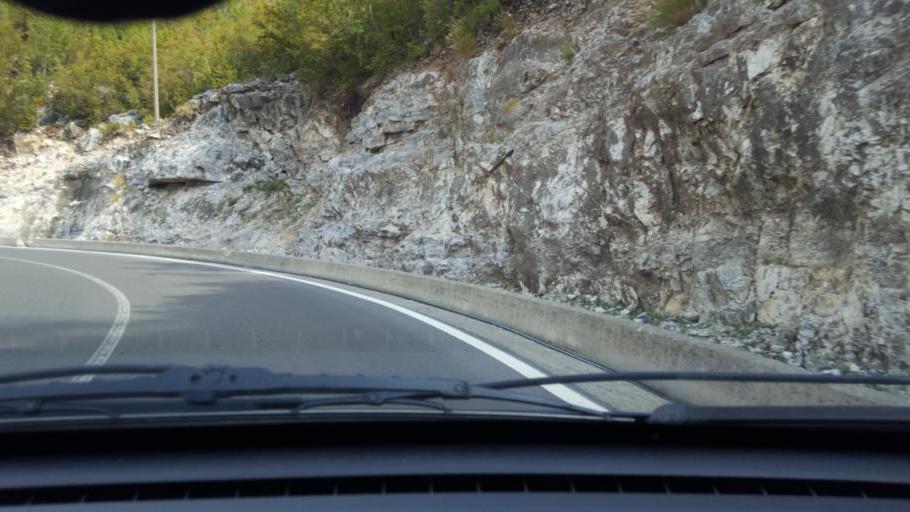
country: AL
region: Shkoder
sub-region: Rrethi i Malesia e Madhe
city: Kastrat
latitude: 42.4240
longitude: 19.5124
